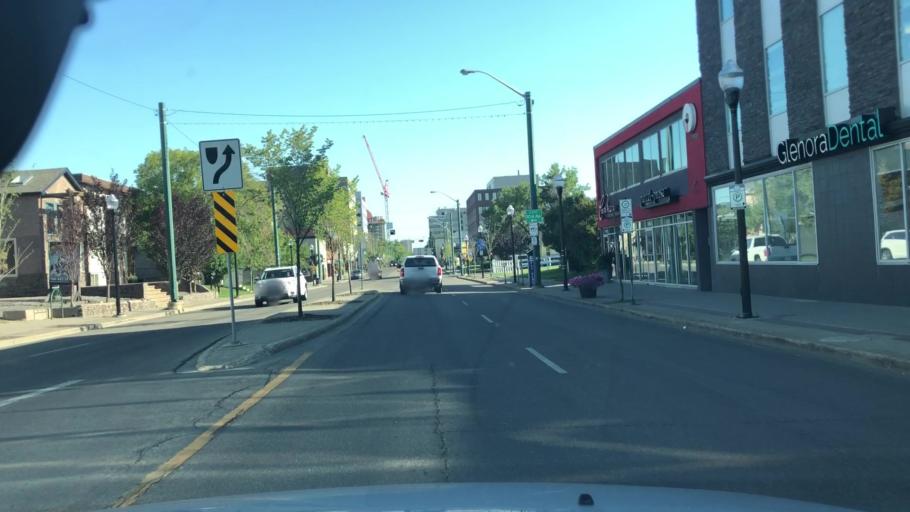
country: CA
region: Alberta
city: Edmonton
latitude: 53.5489
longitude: -113.5359
